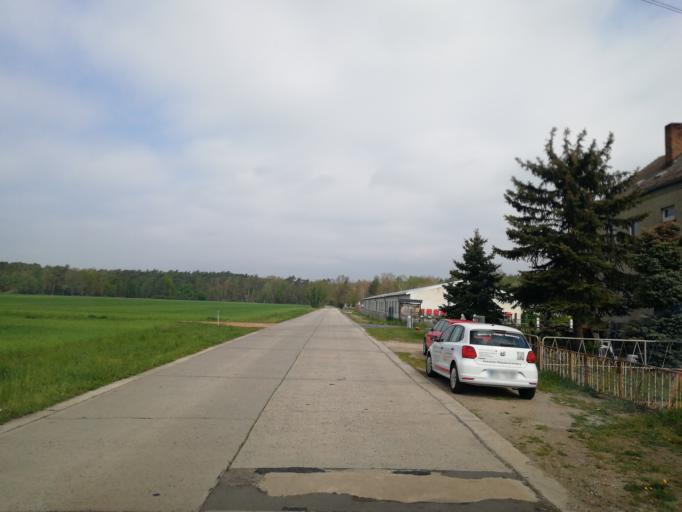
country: DE
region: Saxony
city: Beilrode
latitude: 51.6509
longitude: 13.1167
